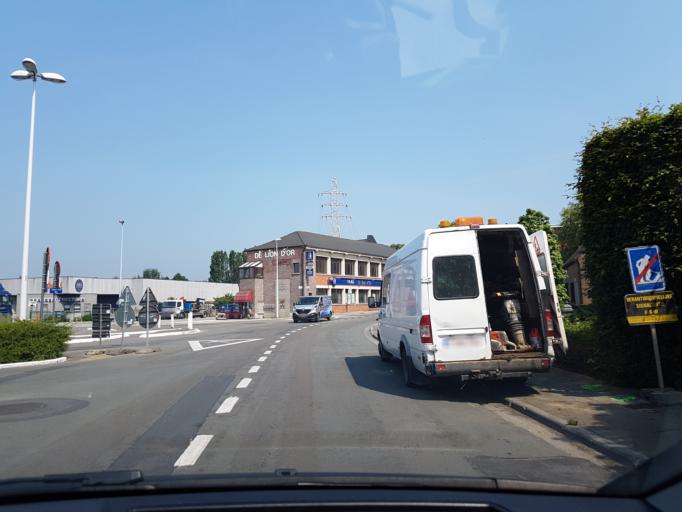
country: BE
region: Flanders
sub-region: Provincie Oost-Vlaanderen
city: Aalst
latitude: 50.9516
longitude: 4.0419
